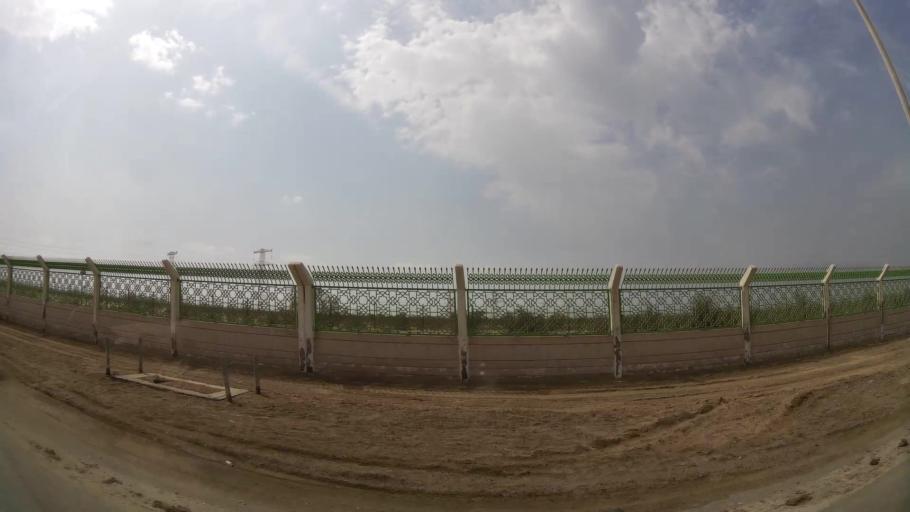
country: AE
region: Abu Dhabi
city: Abu Dhabi
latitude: 24.5273
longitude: 54.6426
